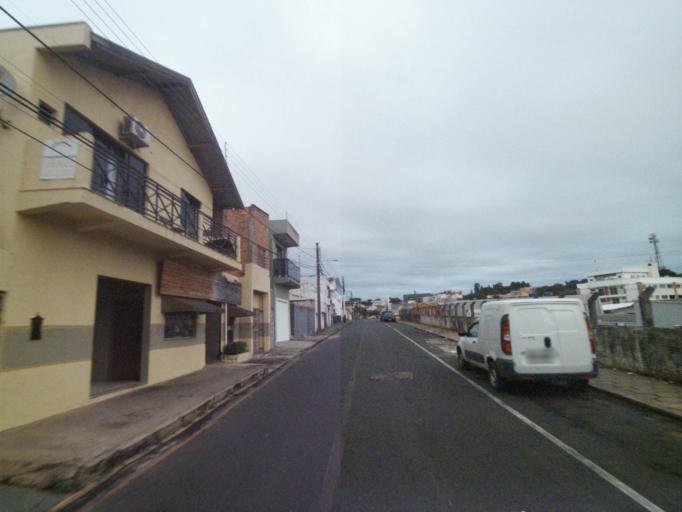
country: BR
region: Parana
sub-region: Telemaco Borba
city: Telemaco Borba
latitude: -24.3231
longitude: -50.6193
